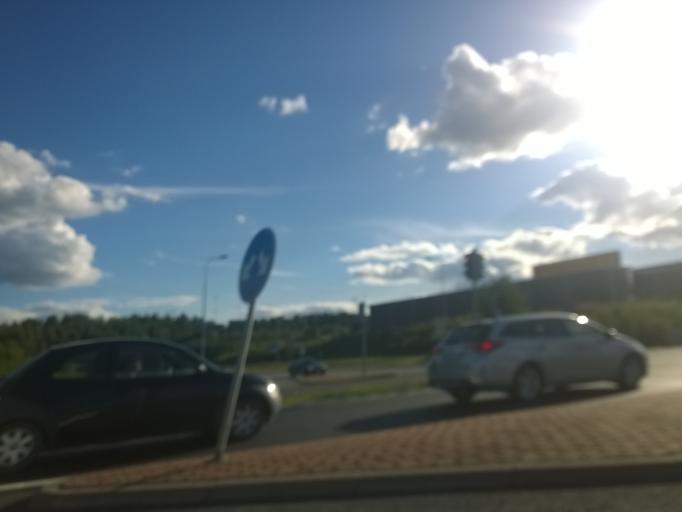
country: FI
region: Pirkanmaa
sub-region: Tampere
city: Tampere
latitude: 61.4649
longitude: 23.7249
